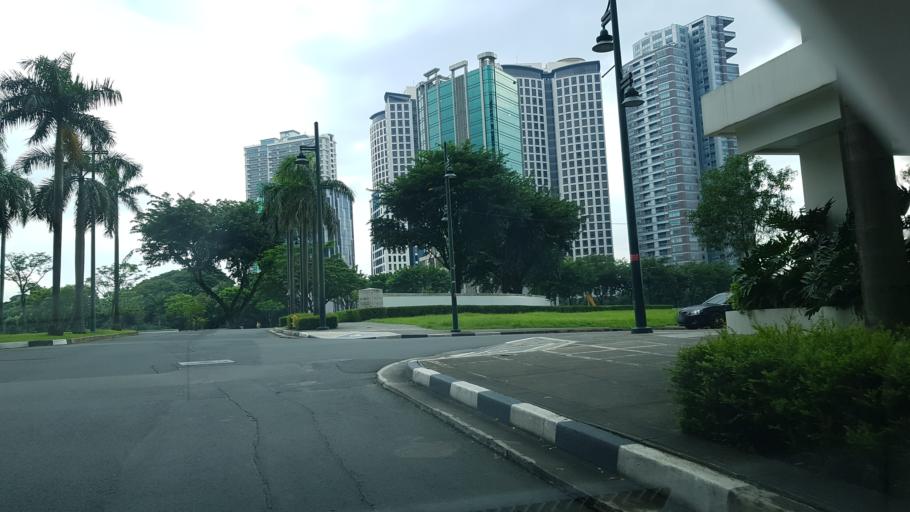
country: PH
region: Metro Manila
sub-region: Makati City
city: Makati City
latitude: 14.5460
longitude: 121.0489
